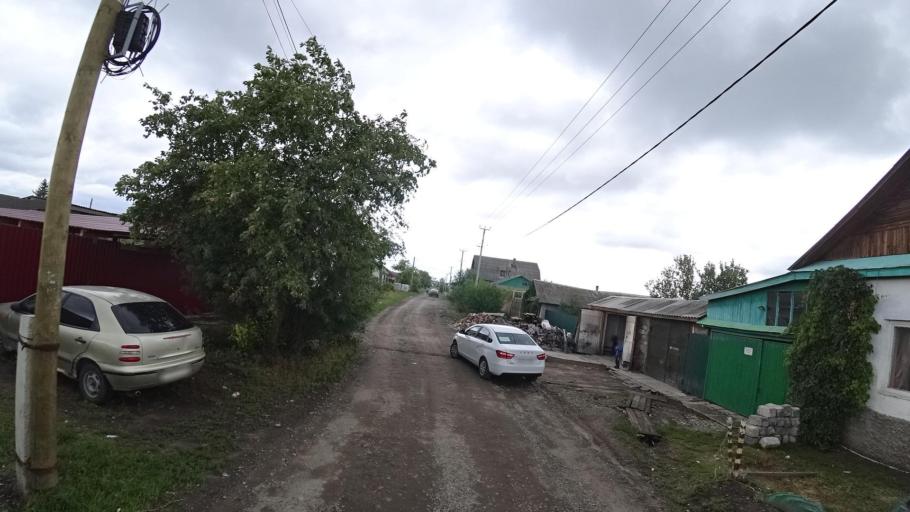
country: RU
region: Sverdlovsk
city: Kamyshlov
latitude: 56.8528
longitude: 62.6876
